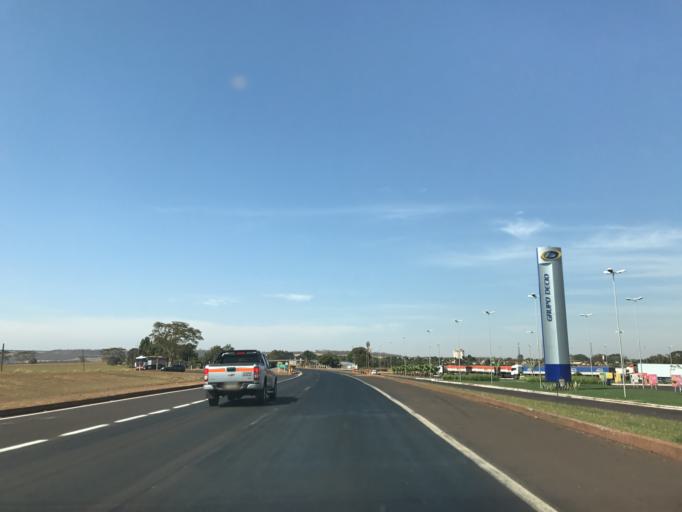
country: BR
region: Minas Gerais
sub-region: Centralina
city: Centralina
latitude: -18.5745
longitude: -49.1939
